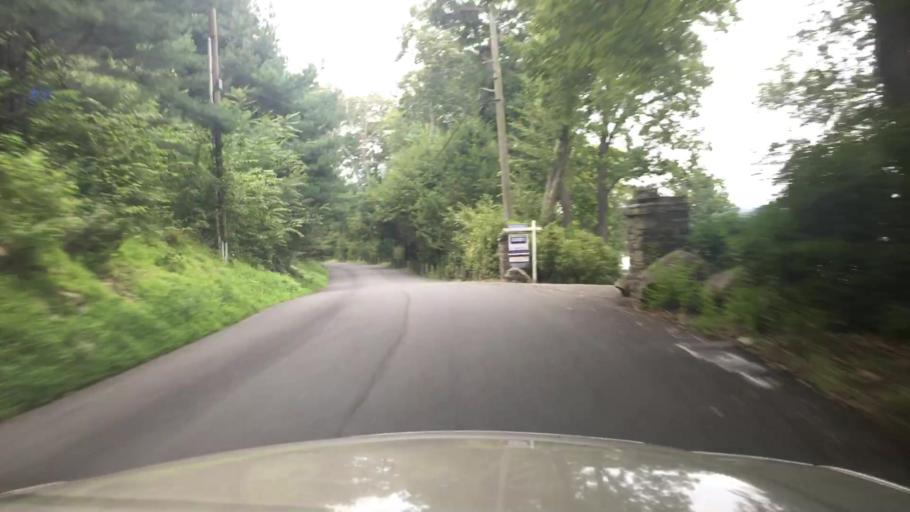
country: US
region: Connecticut
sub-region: Middlesex County
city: Deep River Center
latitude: 41.3863
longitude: -72.4061
